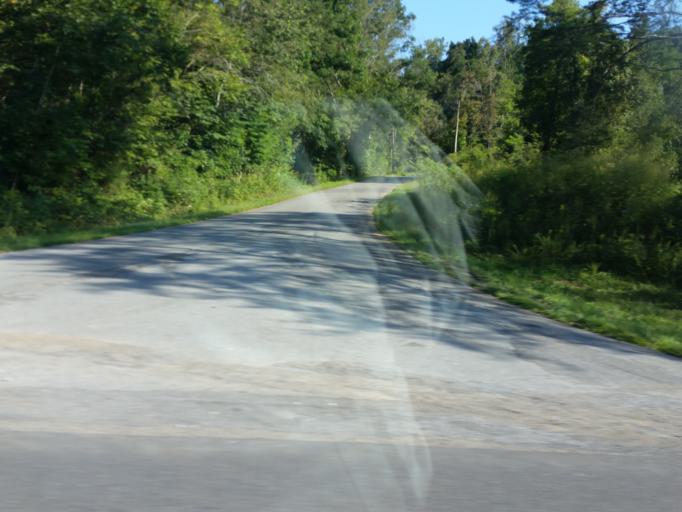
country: US
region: Tennessee
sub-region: Union County
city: Condon
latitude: 36.1977
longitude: -83.8070
